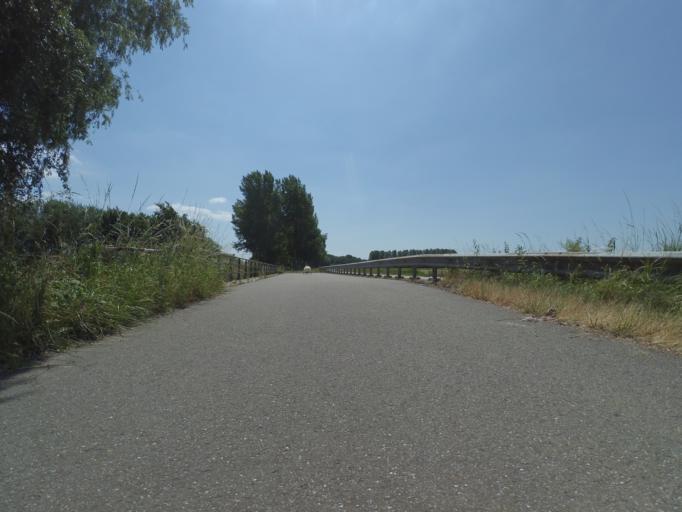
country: NL
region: North Brabant
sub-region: Gemeente Woensdrecht
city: Woensdrecht
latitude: 51.4353
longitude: 4.2801
